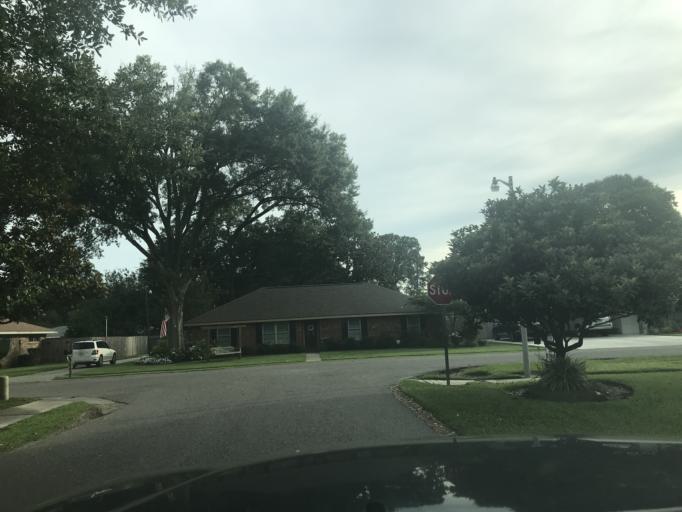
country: US
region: Louisiana
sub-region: Lafayette Parish
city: Lafayette
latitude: 30.1922
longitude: -92.0485
